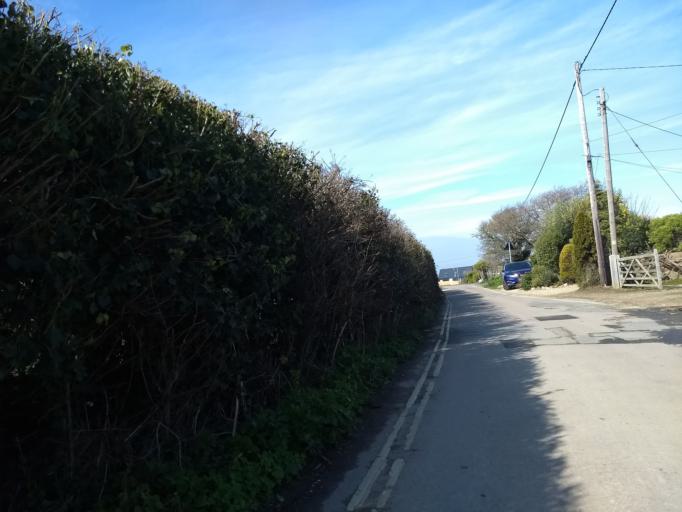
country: GB
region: England
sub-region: Isle of Wight
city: Bembridge
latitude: 50.6827
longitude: -1.0751
